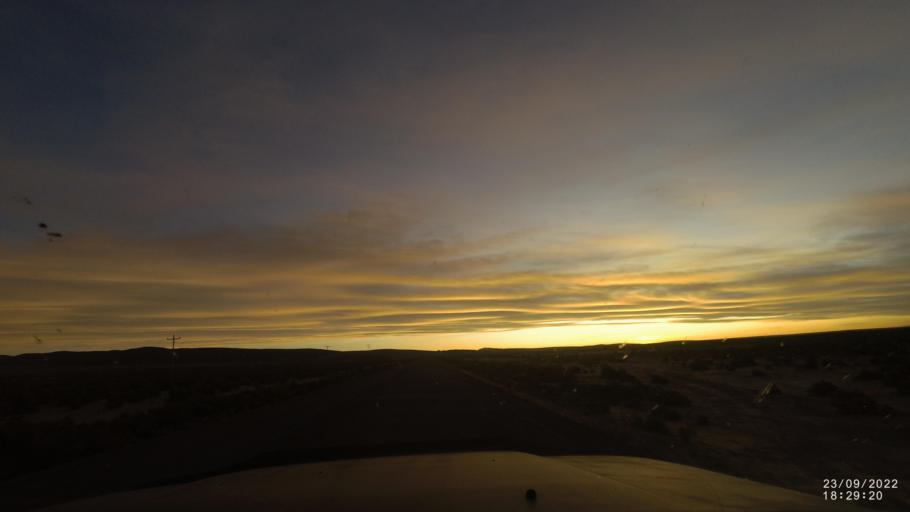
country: BO
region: Oruro
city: Challapata
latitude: -19.3443
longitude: -67.1906
